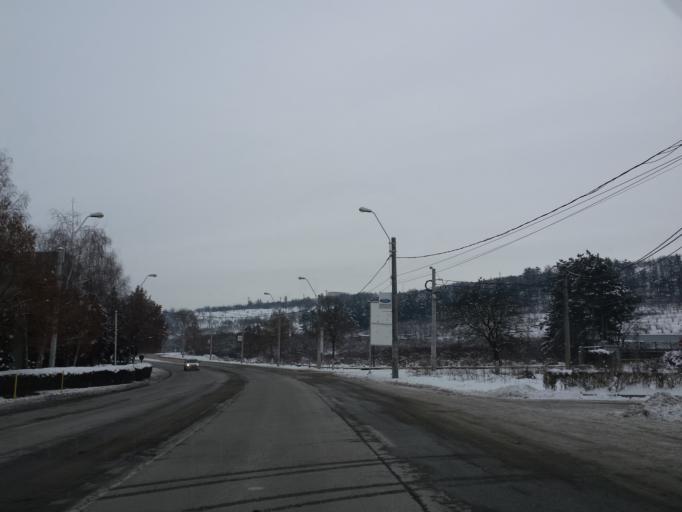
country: RO
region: Hunedoara
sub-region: Municipiul Deva
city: Deva
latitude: 45.8603
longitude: 22.9215
